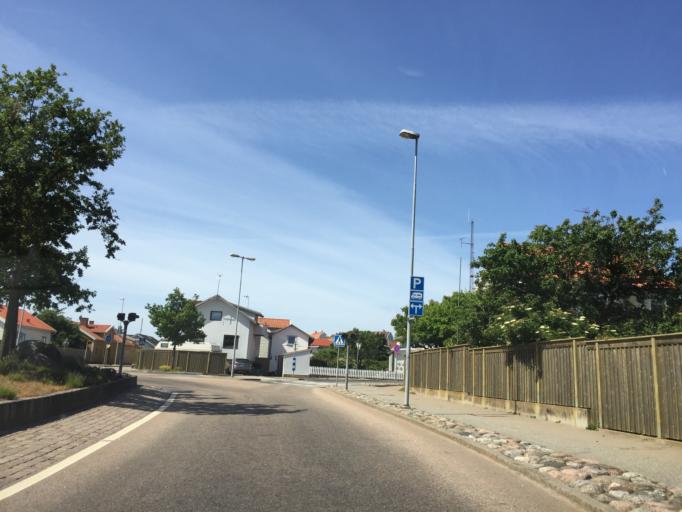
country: SE
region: Vaestra Goetaland
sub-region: Lysekils Kommun
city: Lysekil
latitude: 58.2770
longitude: 11.4454
